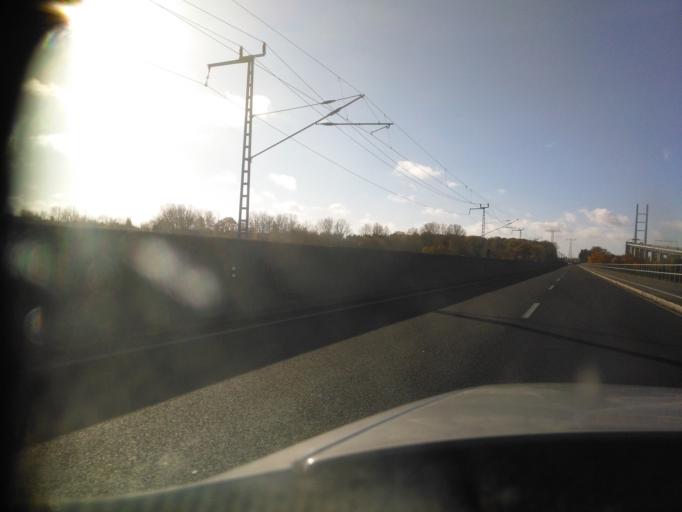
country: DE
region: Mecklenburg-Vorpommern
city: Altefahr
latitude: 54.3145
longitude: 13.1251
